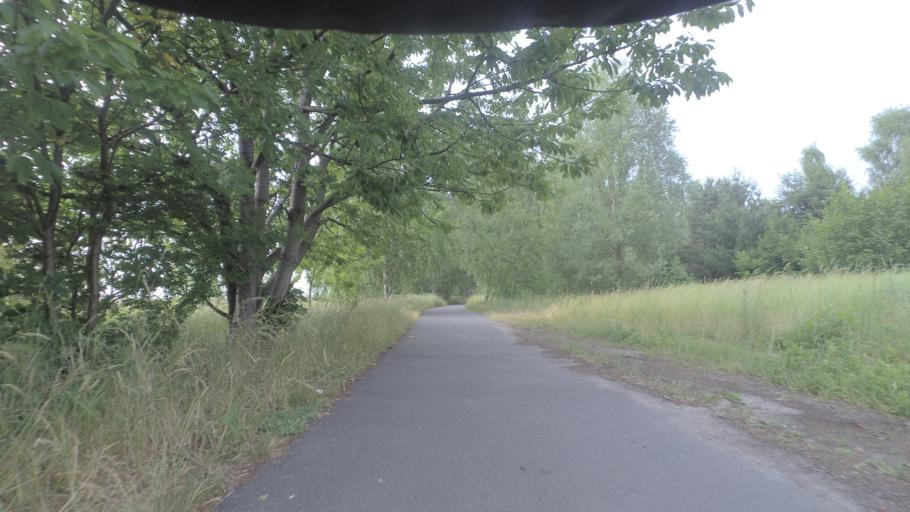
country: DE
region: Berlin
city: Gropiusstadt
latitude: 52.4090
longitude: 13.4727
